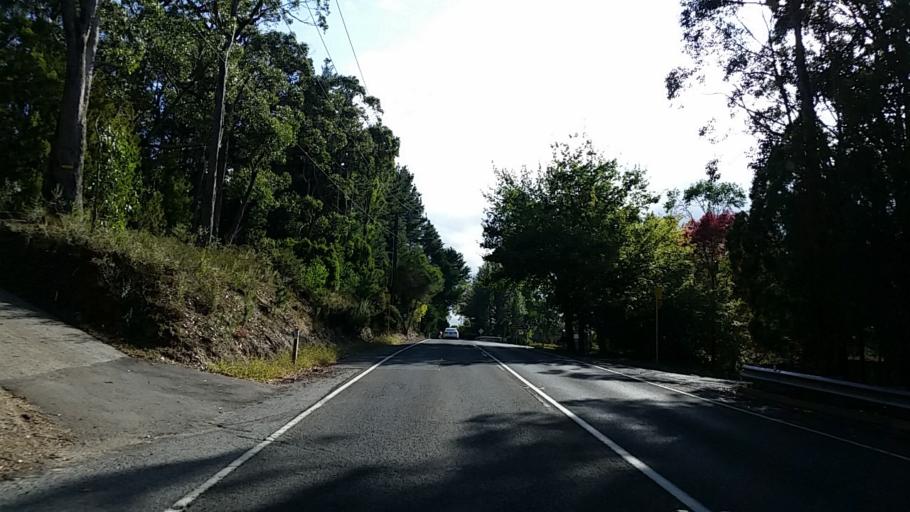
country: AU
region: South Australia
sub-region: Adelaide Hills
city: Crafers
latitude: -34.9889
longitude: 138.7080
